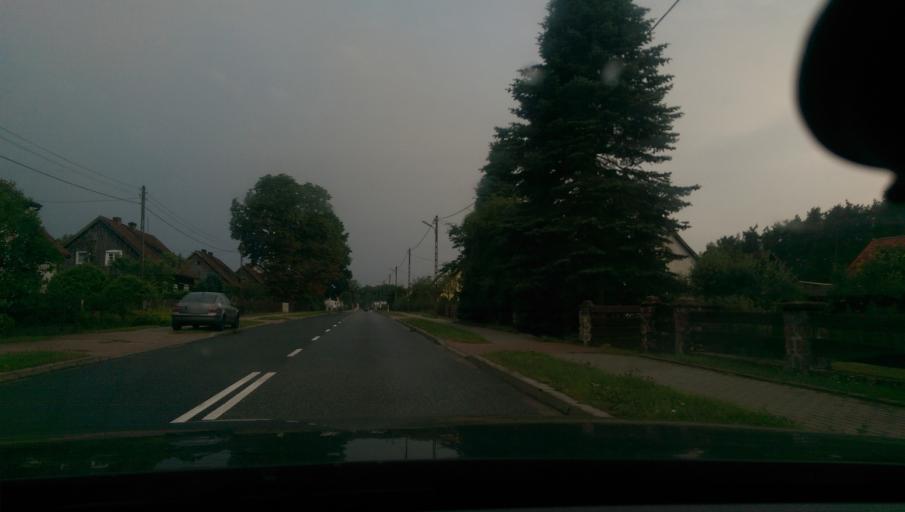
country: PL
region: Warmian-Masurian Voivodeship
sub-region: Powiat szczycienski
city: Rozogi
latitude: 53.6044
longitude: 21.3500
